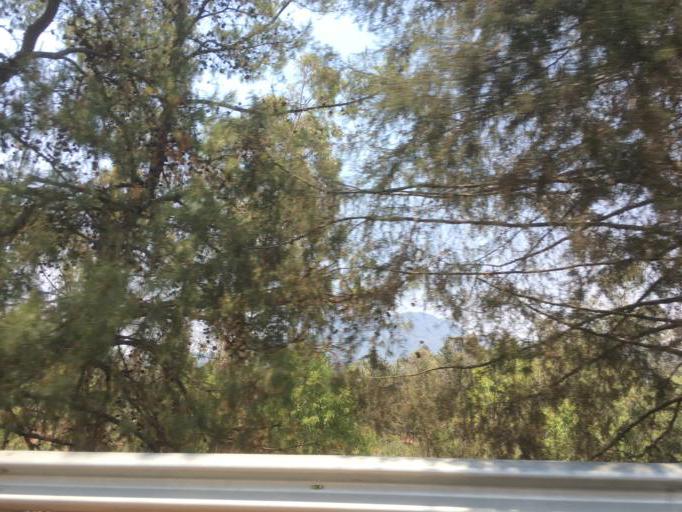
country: MX
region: Michoacan
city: Quiroga
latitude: 19.6544
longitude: -101.4957
